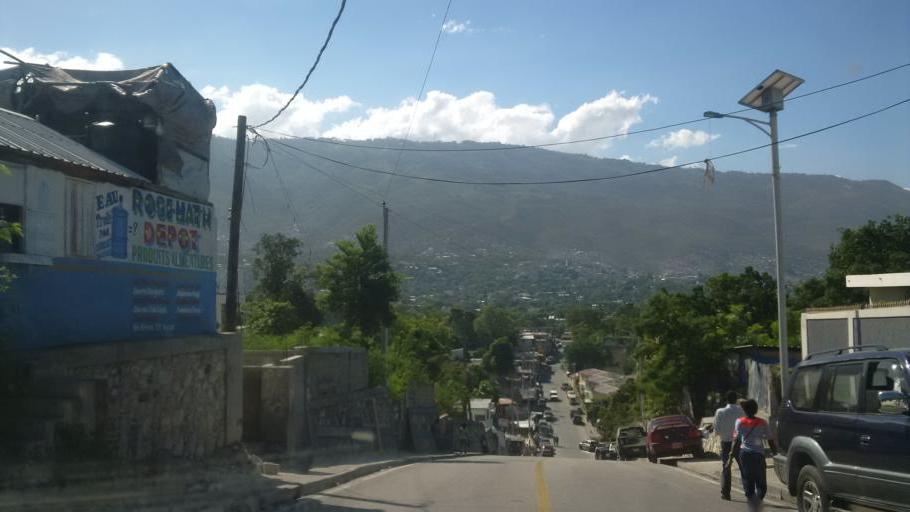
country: HT
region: Ouest
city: Port-au-Prince
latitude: 18.5434
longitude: -72.3251
